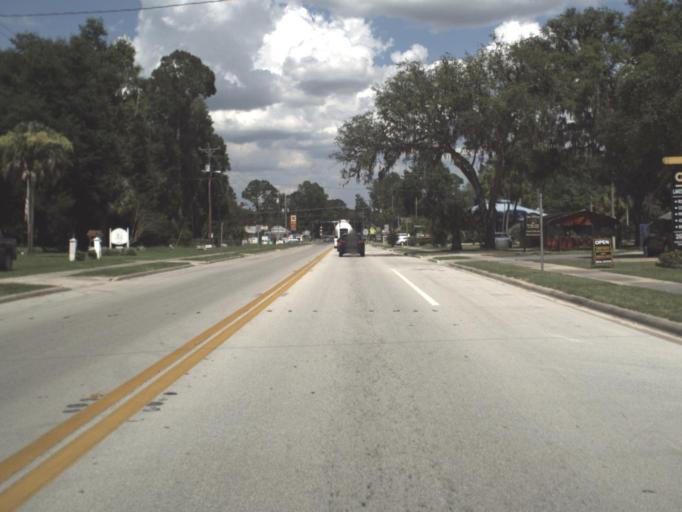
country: US
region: Florida
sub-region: Clay County
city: Keystone Heights
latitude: 29.7097
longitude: -82.0472
